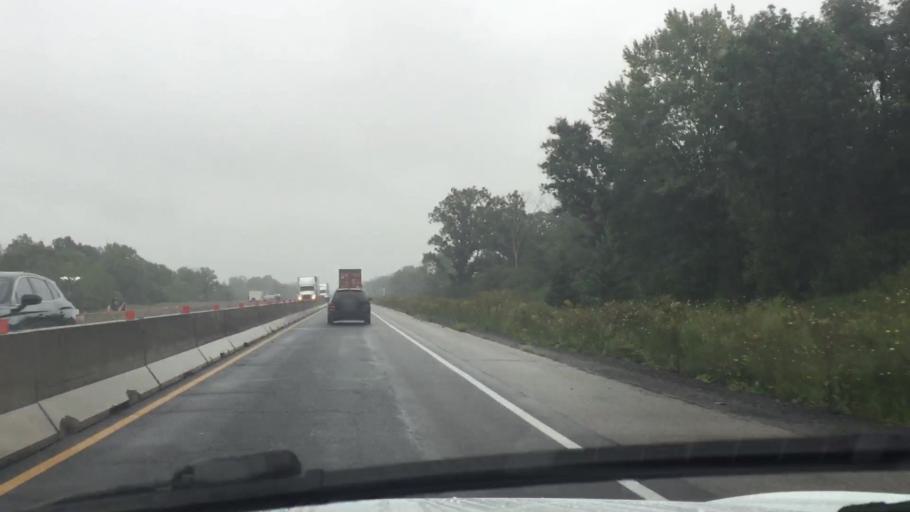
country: CA
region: Ontario
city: Delaware
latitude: 42.8044
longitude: -81.3331
